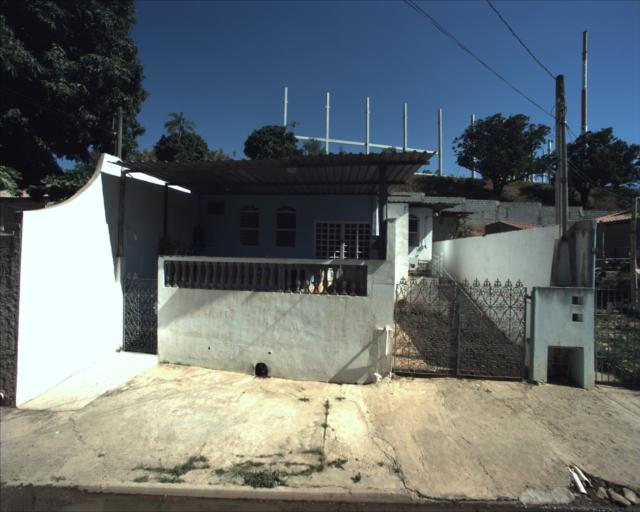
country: BR
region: Sao Paulo
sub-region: Sorocaba
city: Sorocaba
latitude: -23.4962
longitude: -47.4166
